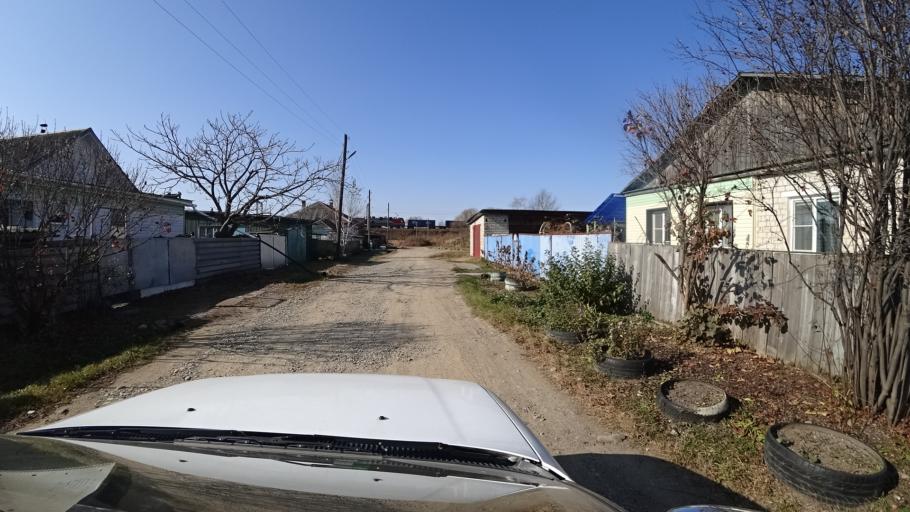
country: RU
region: Primorskiy
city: Dal'nerechensk
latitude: 45.9297
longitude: 133.7139
